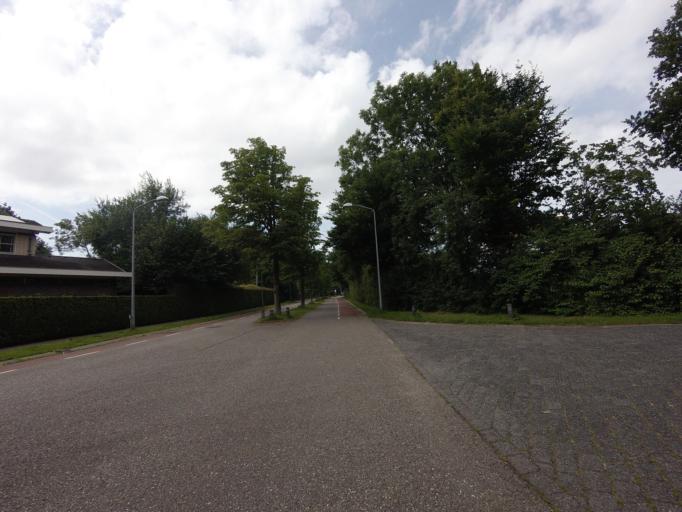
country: NL
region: North Holland
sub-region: Gemeente Huizen
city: Huizen
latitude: 52.3430
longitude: 5.2988
